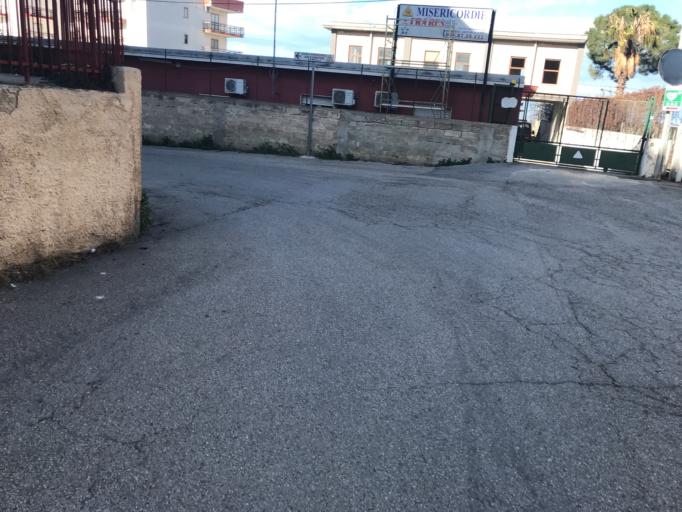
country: IT
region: Apulia
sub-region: Provincia di Bari
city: Corato
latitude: 41.1580
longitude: 16.4155
